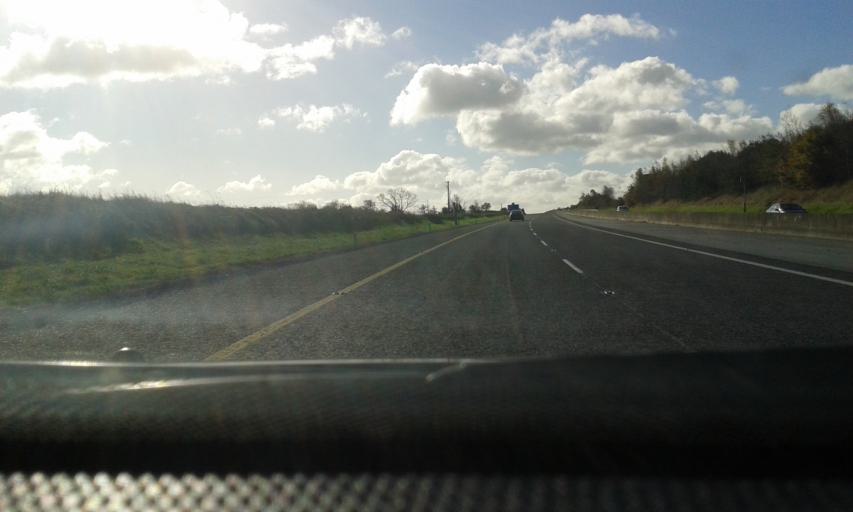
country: IE
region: Munster
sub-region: County Cork
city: Fermoy
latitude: 52.1078
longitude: -8.2753
